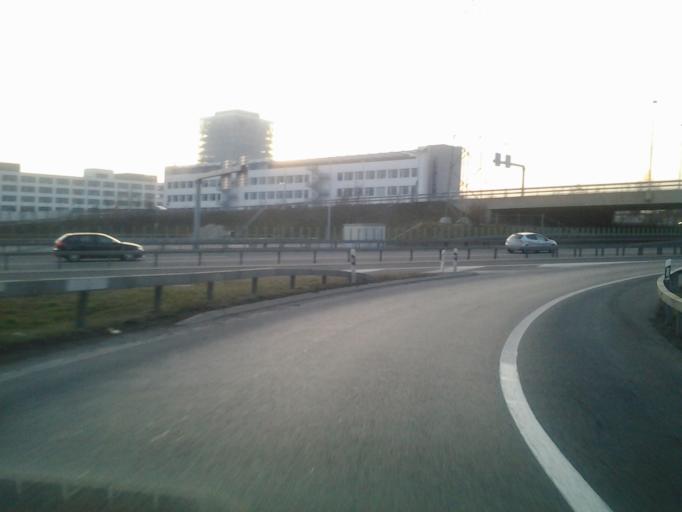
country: CH
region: Zug
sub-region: Zug
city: Hunenberg
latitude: 47.1510
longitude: 8.4377
